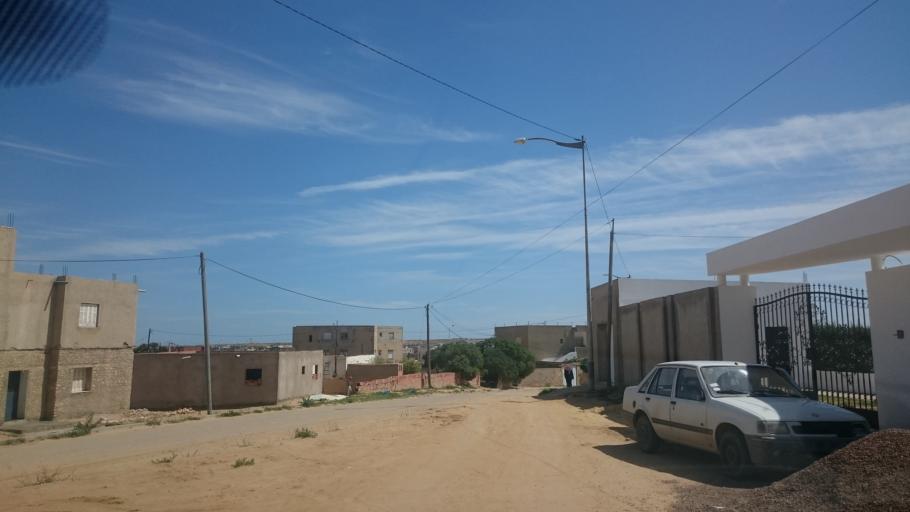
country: TN
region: Safaqis
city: Sfax
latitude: 34.7454
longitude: 10.5185
